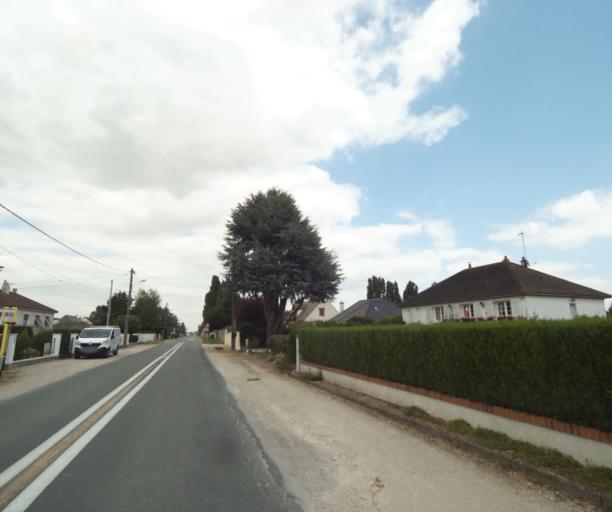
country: FR
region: Centre
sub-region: Departement du Loiret
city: Boigny-sur-Bionne
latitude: 47.9190
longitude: 2.0428
